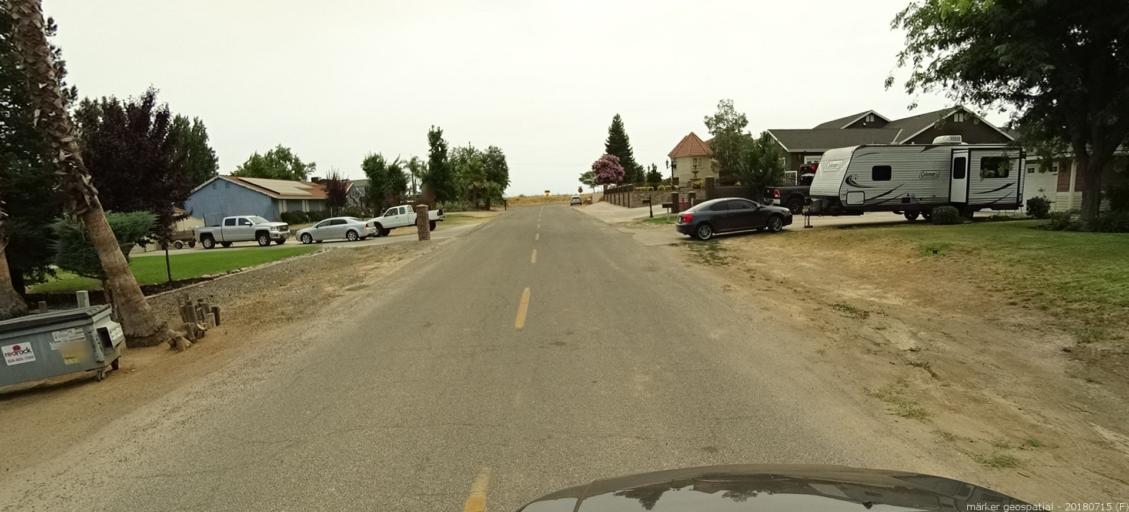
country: US
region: California
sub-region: Madera County
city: Madera Acres
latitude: 37.0207
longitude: -120.0576
